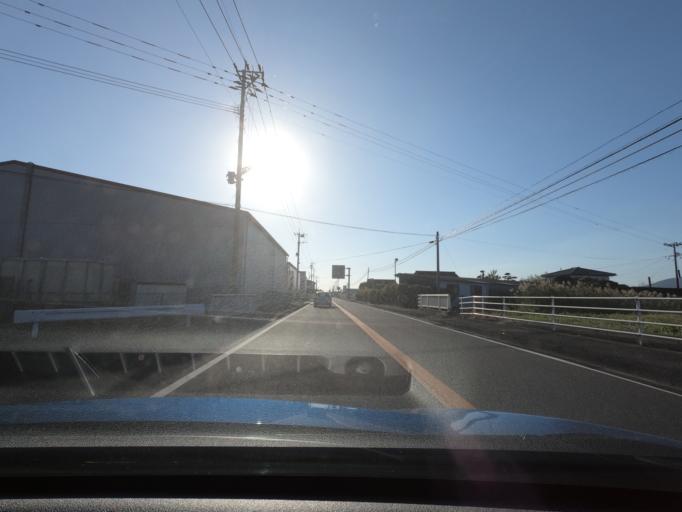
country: JP
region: Kagoshima
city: Izumi
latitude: 32.0923
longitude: 130.2933
